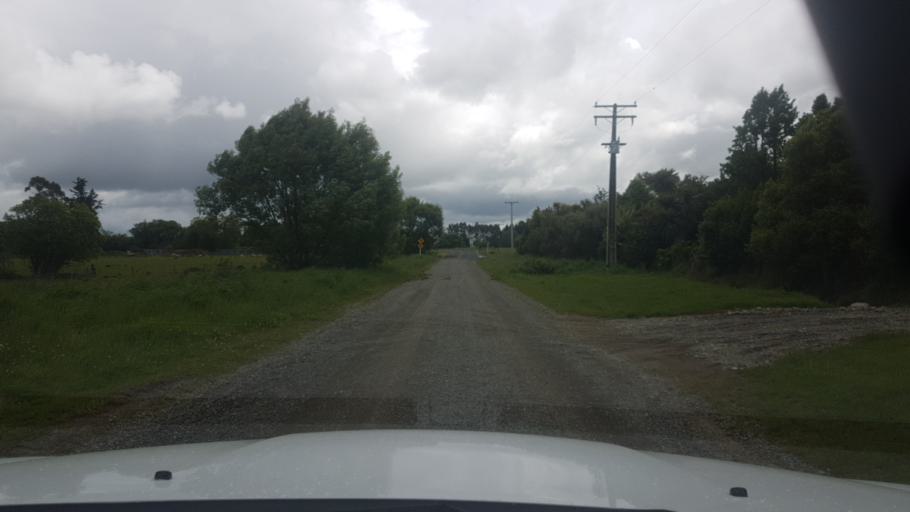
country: NZ
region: Canterbury
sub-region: Timaru District
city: Pleasant Point
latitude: -44.2511
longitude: 171.2626
